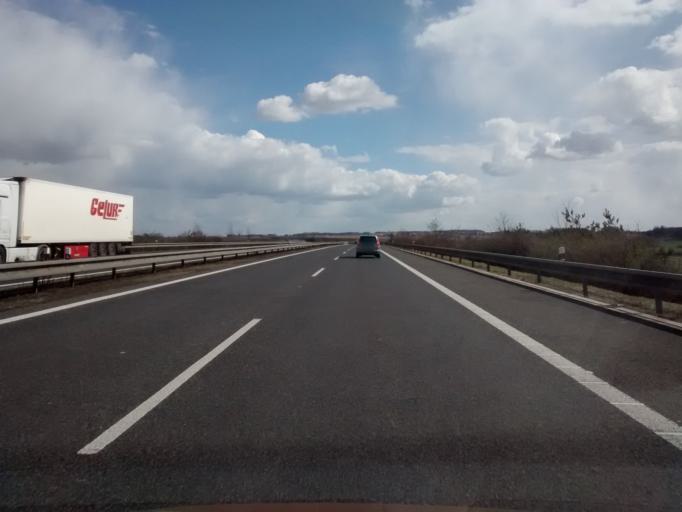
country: CZ
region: Ustecky
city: Roudnice nad Labem
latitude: 50.3635
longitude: 14.2634
